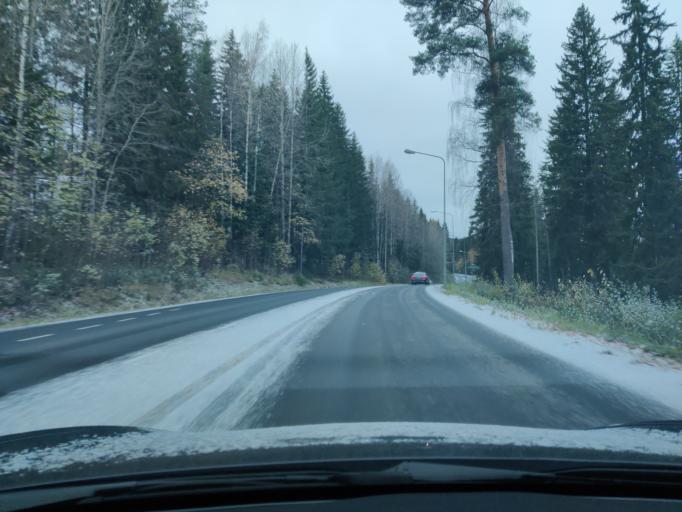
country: FI
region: Northern Savo
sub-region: Kuopio
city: Kuopio
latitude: 62.8426
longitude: 27.6329
